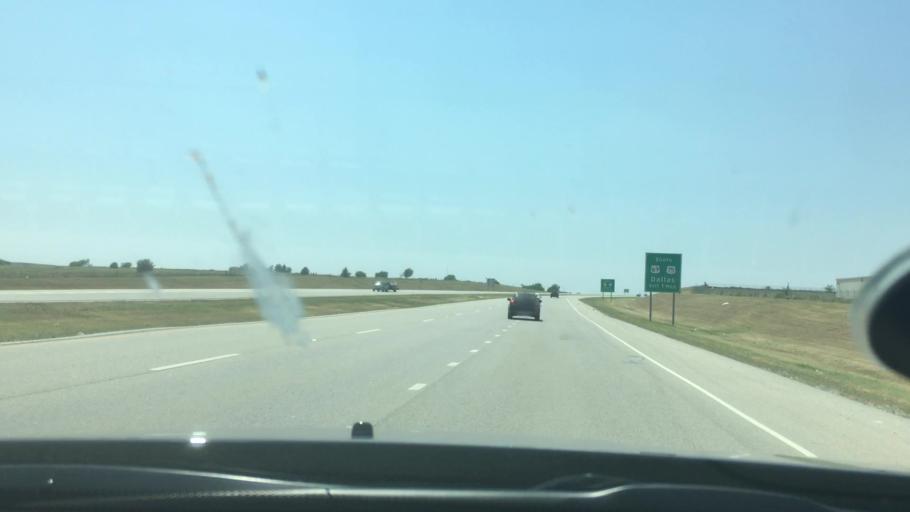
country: US
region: Oklahoma
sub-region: Bryan County
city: Calera
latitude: 33.9657
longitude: -96.4016
